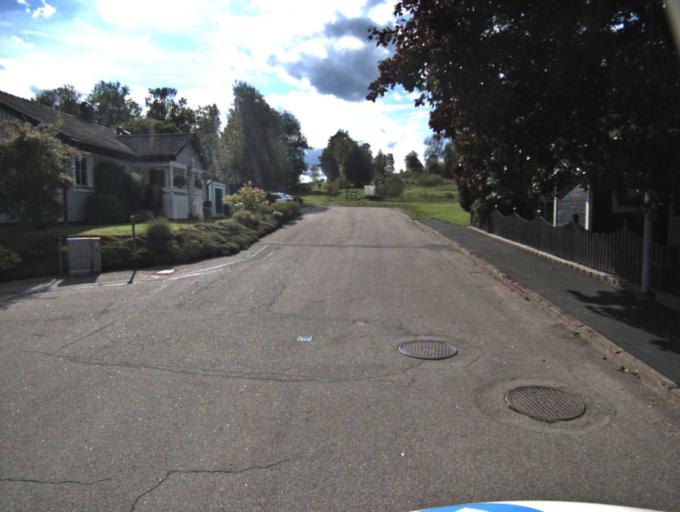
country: SE
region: Vaestra Goetaland
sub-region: Ulricehamns Kommun
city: Ulricehamn
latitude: 57.9318
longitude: 13.4862
